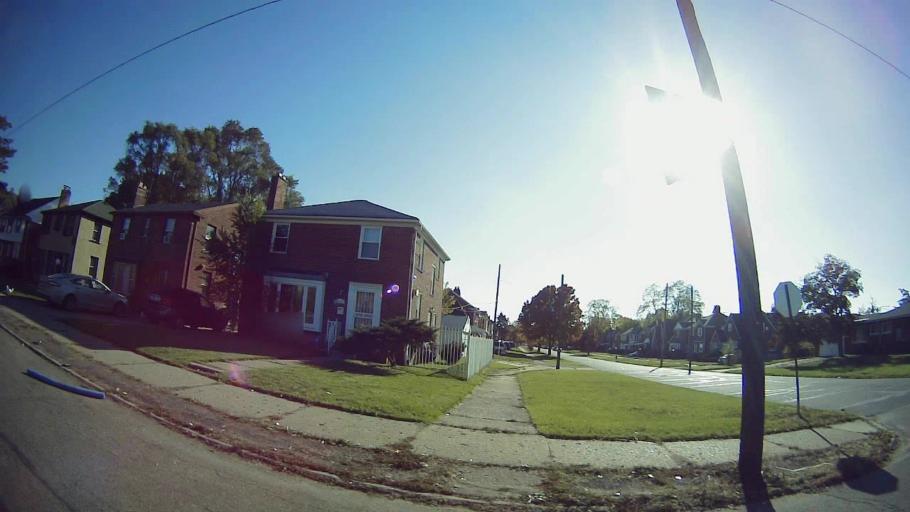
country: US
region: Michigan
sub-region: Oakland County
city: Ferndale
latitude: 42.4313
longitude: -83.1553
